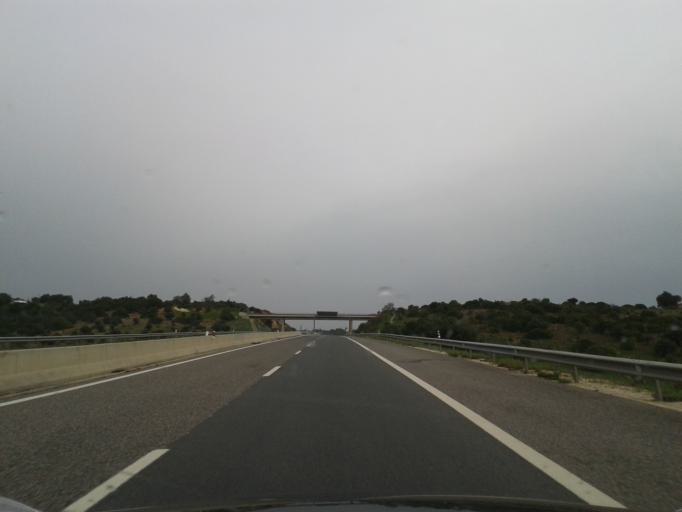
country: PT
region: Faro
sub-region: Portimao
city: Alvor
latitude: 37.1804
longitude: -8.6045
